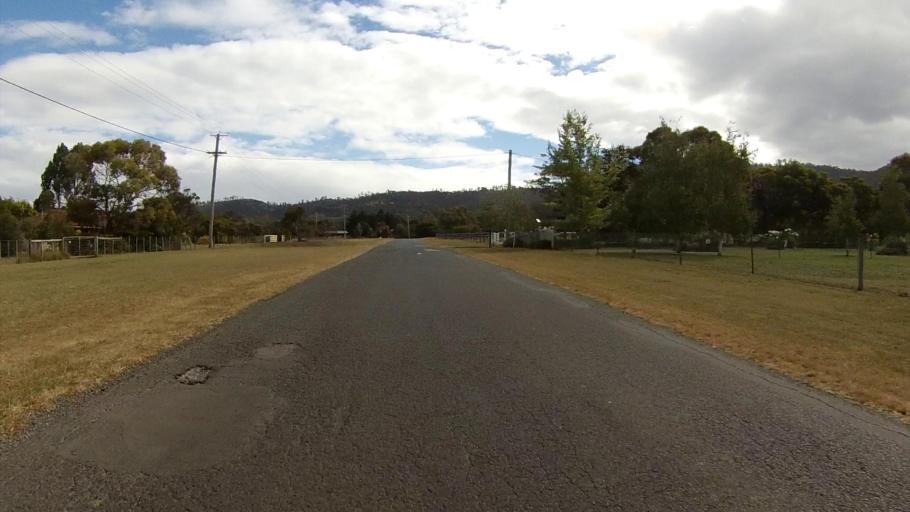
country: AU
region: Tasmania
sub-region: Clarence
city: Acton Park
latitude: -42.8651
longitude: 147.4844
